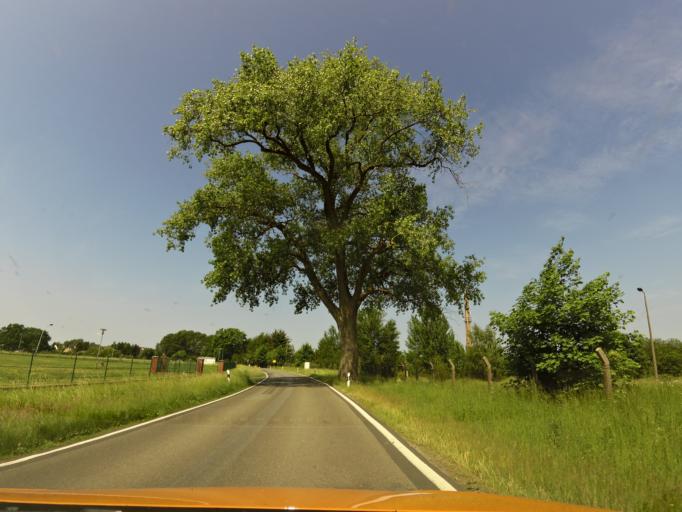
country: DE
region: Mecklenburg-Vorpommern
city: Parchim
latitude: 53.4223
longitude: 11.8698
